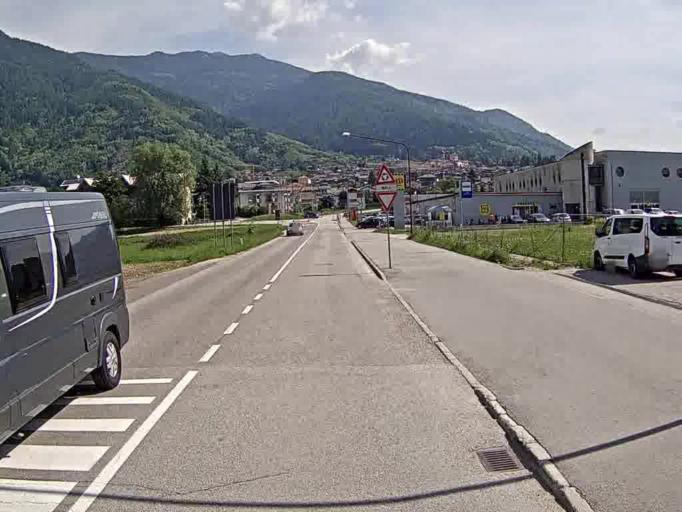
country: IT
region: Trentino-Alto Adige
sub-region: Provincia di Trento
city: Levico Terme
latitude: 46.0062
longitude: 11.2917
